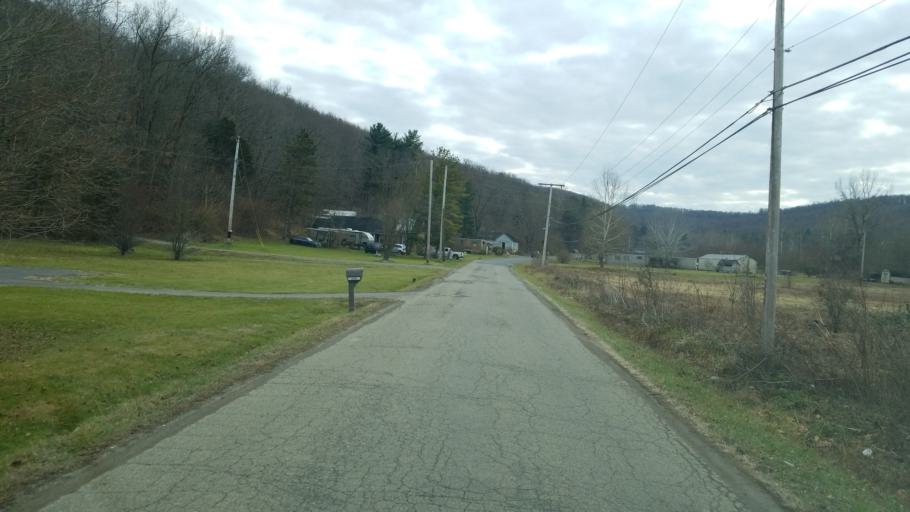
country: US
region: Ohio
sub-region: Highland County
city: Greenfield
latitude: 39.2220
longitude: -83.2689
